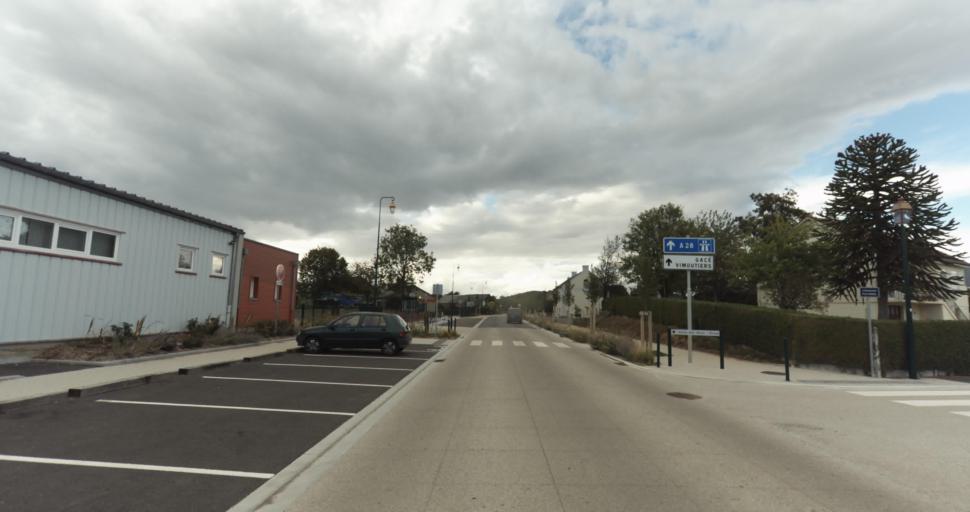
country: FR
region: Lower Normandy
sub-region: Departement de l'Orne
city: Sainte-Gauburge-Sainte-Colombe
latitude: 48.7415
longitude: 0.3880
